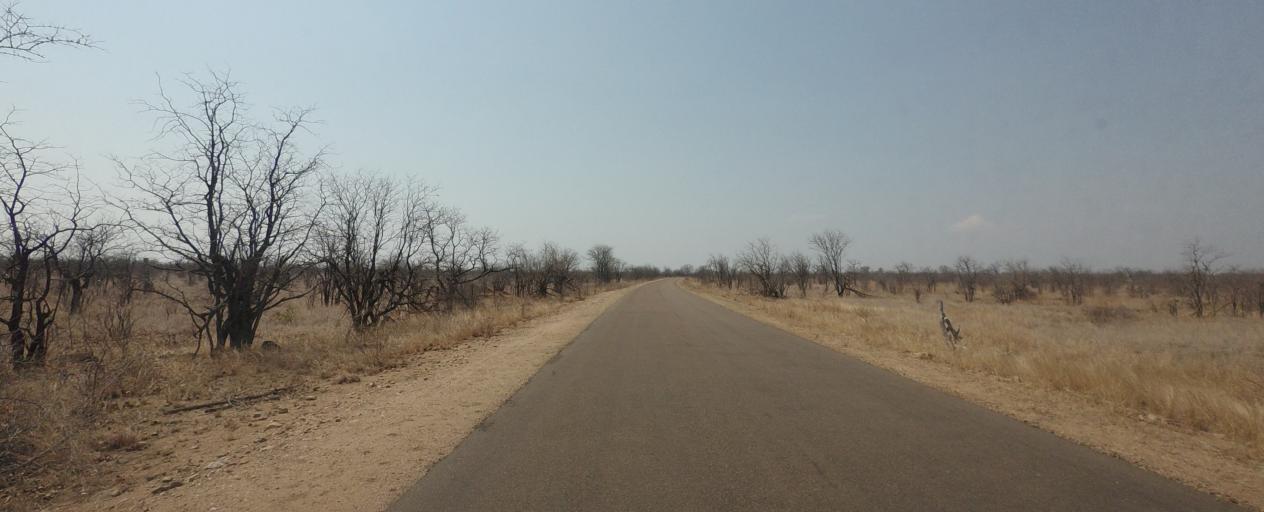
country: ZA
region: Limpopo
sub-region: Mopani District Municipality
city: Giyani
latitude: -23.3491
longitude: 31.3190
